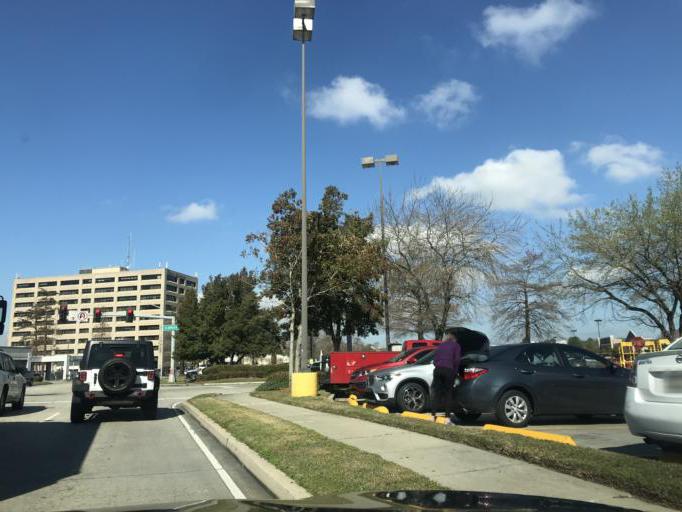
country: US
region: Louisiana
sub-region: Jefferson Parish
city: Elmwood
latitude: 29.9640
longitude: -90.1871
